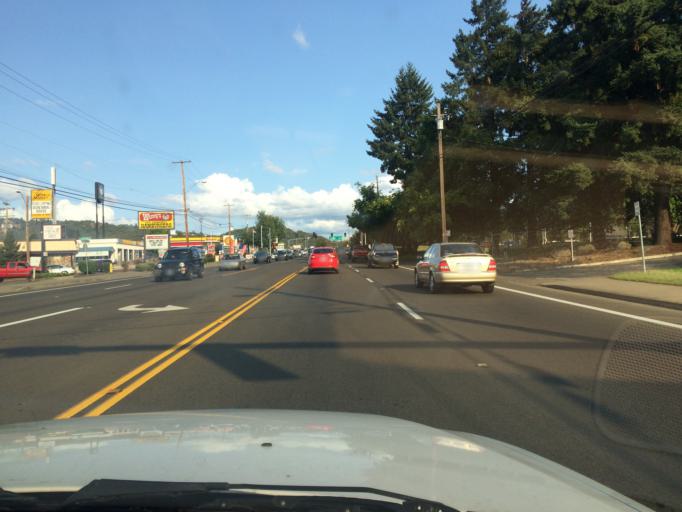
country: US
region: Oregon
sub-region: Douglas County
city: Roseburg
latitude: 43.2285
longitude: -123.3670
